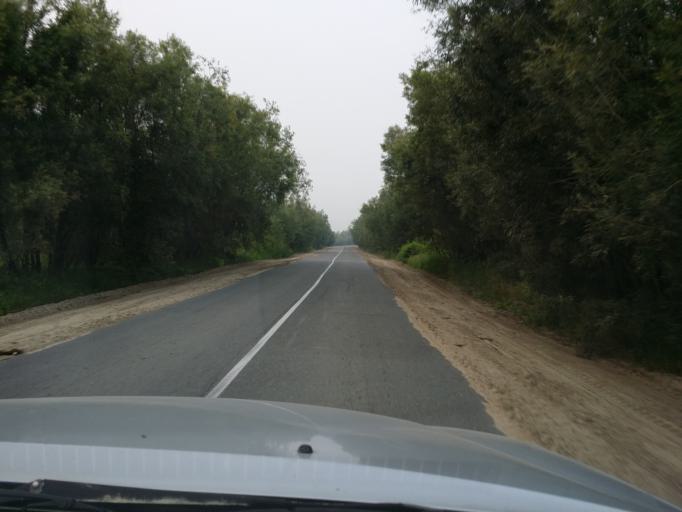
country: RU
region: Khanty-Mansiyskiy Avtonomnyy Okrug
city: Megion
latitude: 60.9987
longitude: 76.3035
